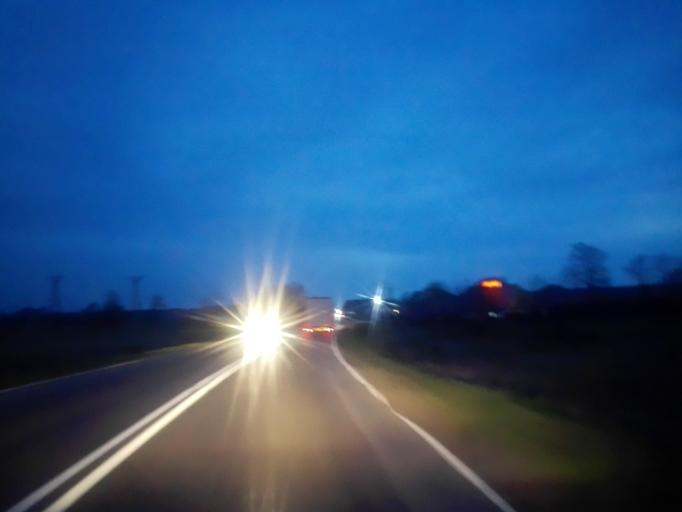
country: PL
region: Podlasie
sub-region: Powiat lomzynski
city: Sniadowo
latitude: 53.0734
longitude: 22.0153
